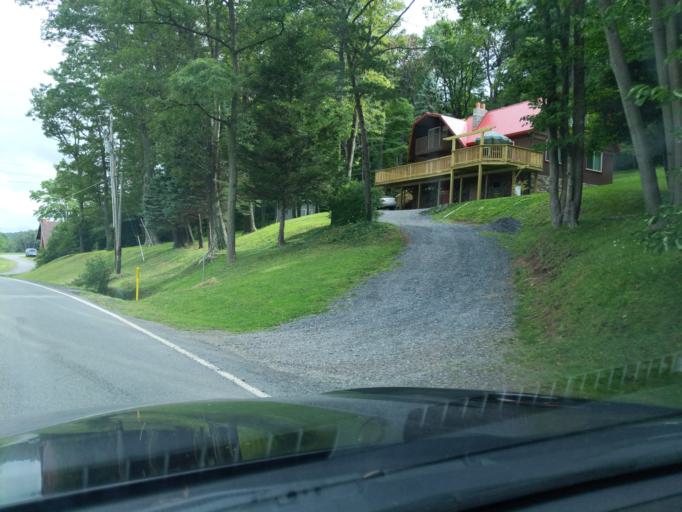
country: US
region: Pennsylvania
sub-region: Cambria County
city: Beaverdale
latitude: 40.2985
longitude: -78.5777
